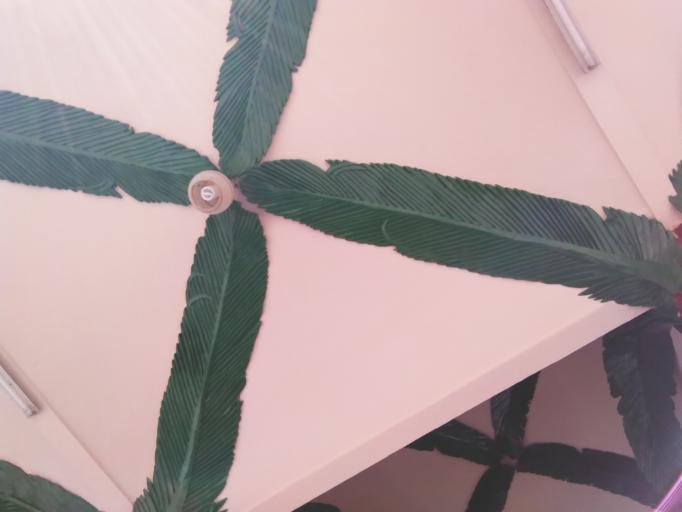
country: BO
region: Cochabamba
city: Sipe Sipe
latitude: -17.4219
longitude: -66.2840
